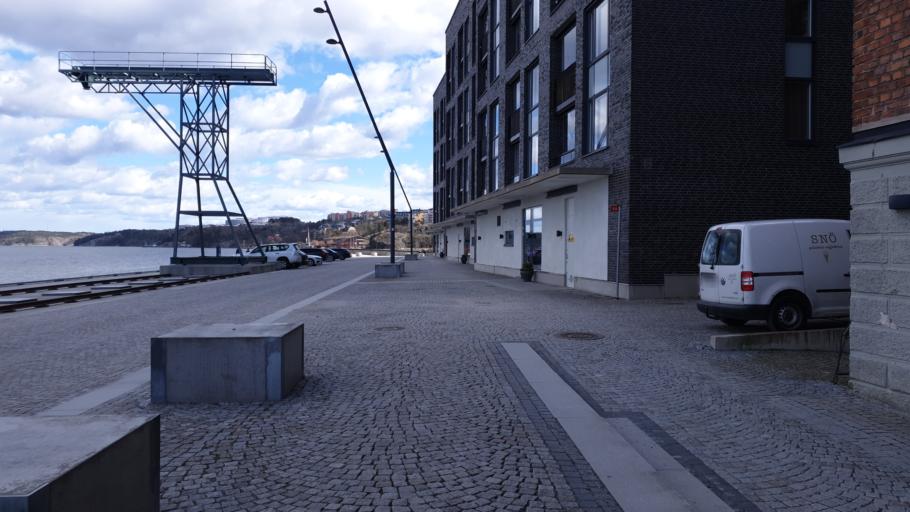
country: SE
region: Stockholm
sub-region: Nacka Kommun
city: Nacka
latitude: 59.3178
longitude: 18.1410
